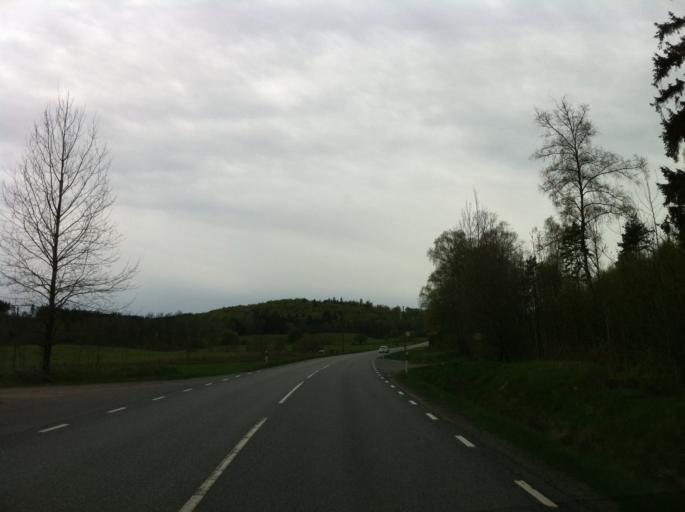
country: SE
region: Halland
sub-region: Falkenbergs Kommun
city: Falkenberg
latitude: 57.1158
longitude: 12.7026
